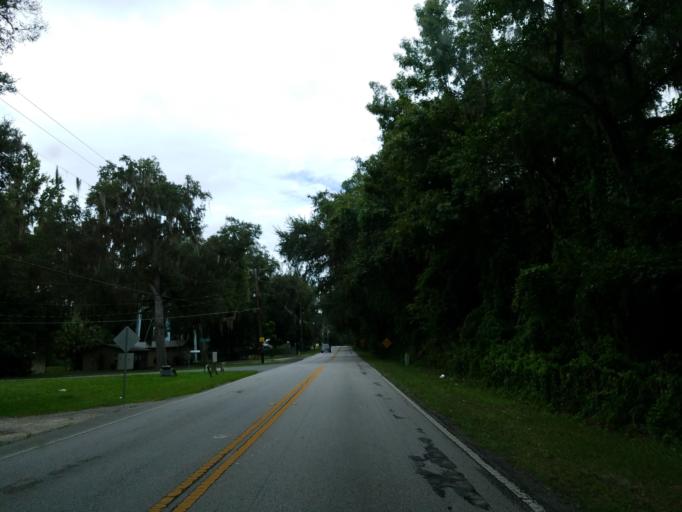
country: US
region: Florida
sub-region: Sumter County
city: Lake Panasoffkee
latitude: 28.7958
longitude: -82.1336
